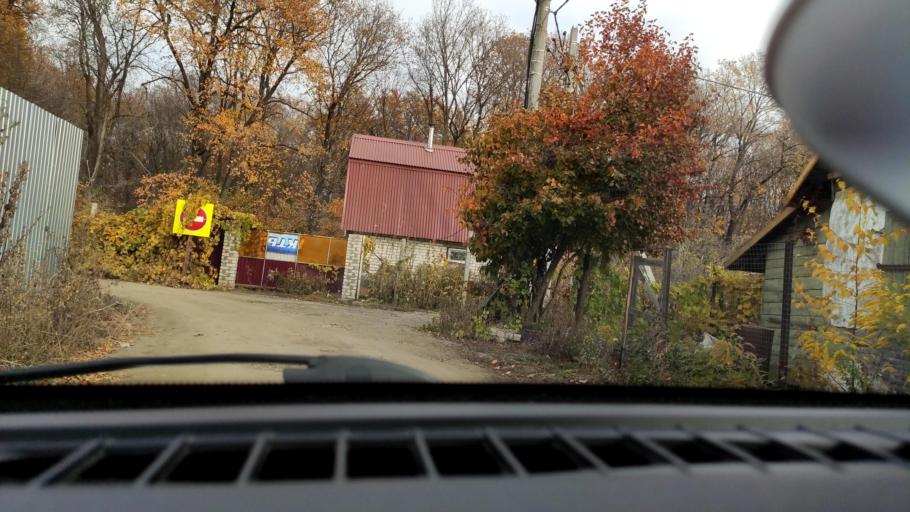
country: RU
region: Samara
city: Petra-Dubrava
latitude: 53.2675
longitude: 50.2636
